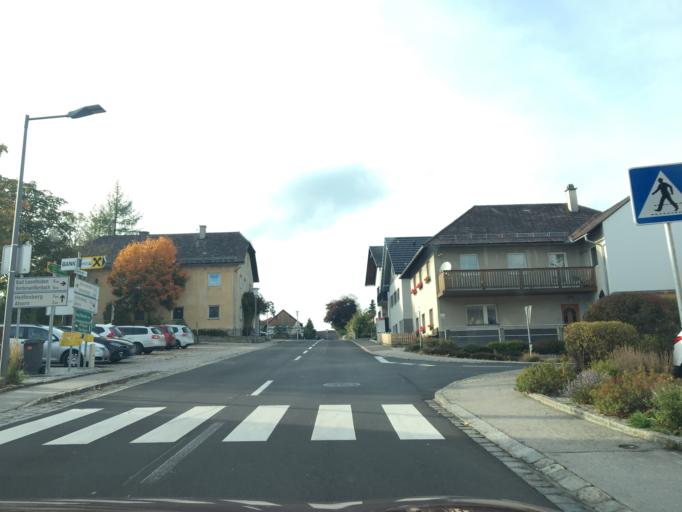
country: AT
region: Upper Austria
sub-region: Politischer Bezirk Urfahr-Umgebung
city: Oberneukirchen
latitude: 48.5141
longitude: 14.2011
